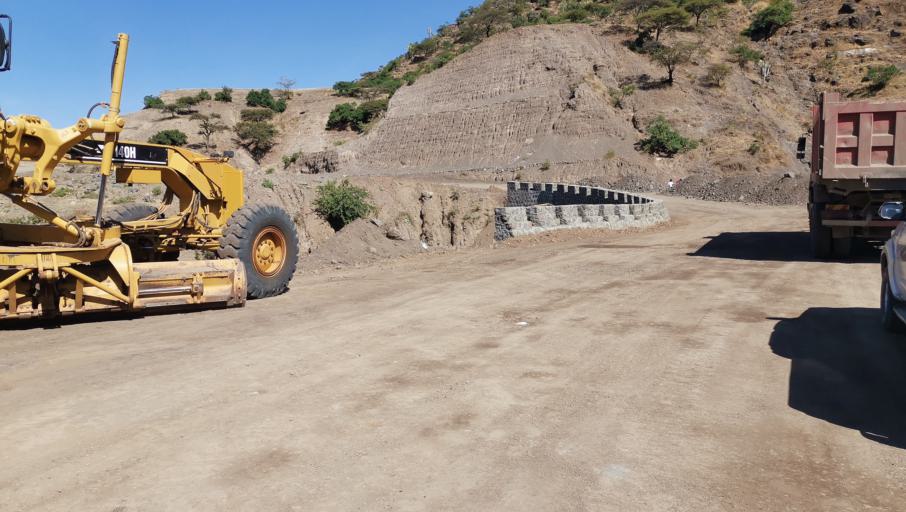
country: ET
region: Amhara
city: Lalibela
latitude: 12.2283
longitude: 39.0312
